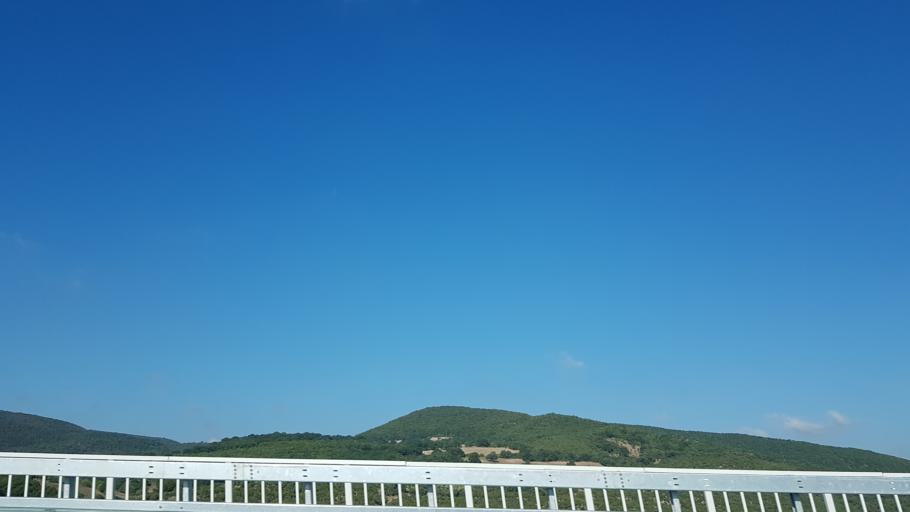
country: TR
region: Balikesir
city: Ertugrul
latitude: 39.5790
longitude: 27.6975
